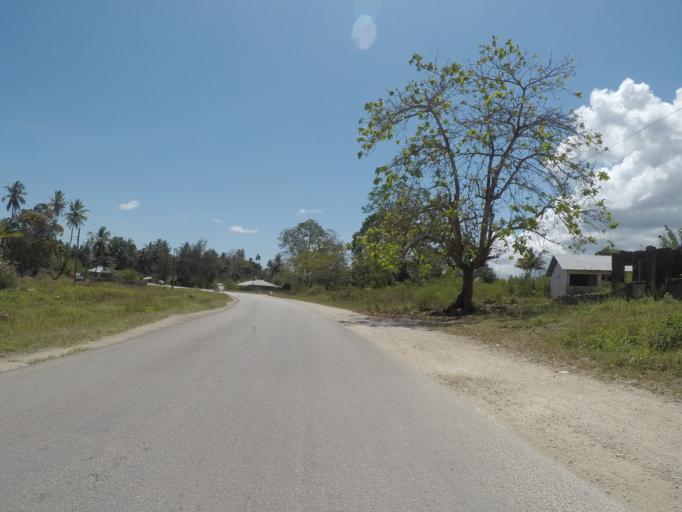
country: TZ
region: Zanzibar Central/South
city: Nganane
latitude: -6.2703
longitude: 39.4277
